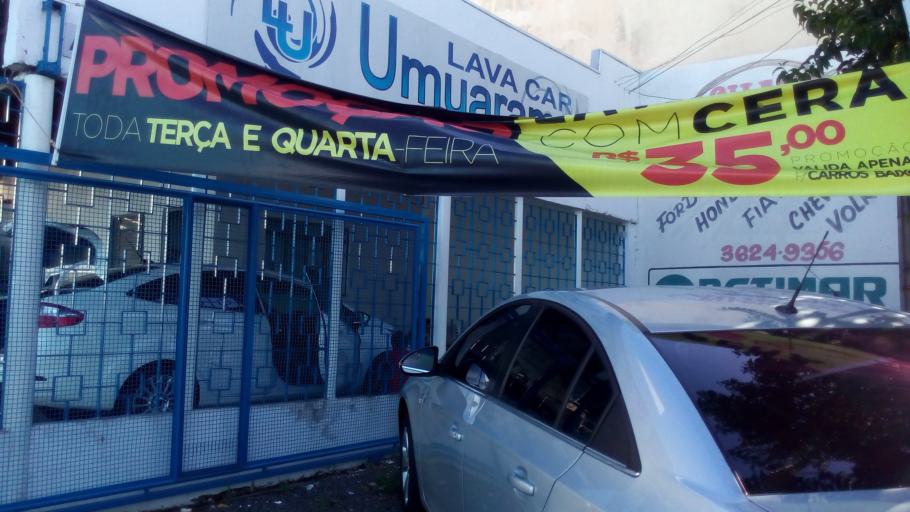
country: BR
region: Parana
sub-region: Umuarama
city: Umuarama
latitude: -23.7604
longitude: -53.3071
